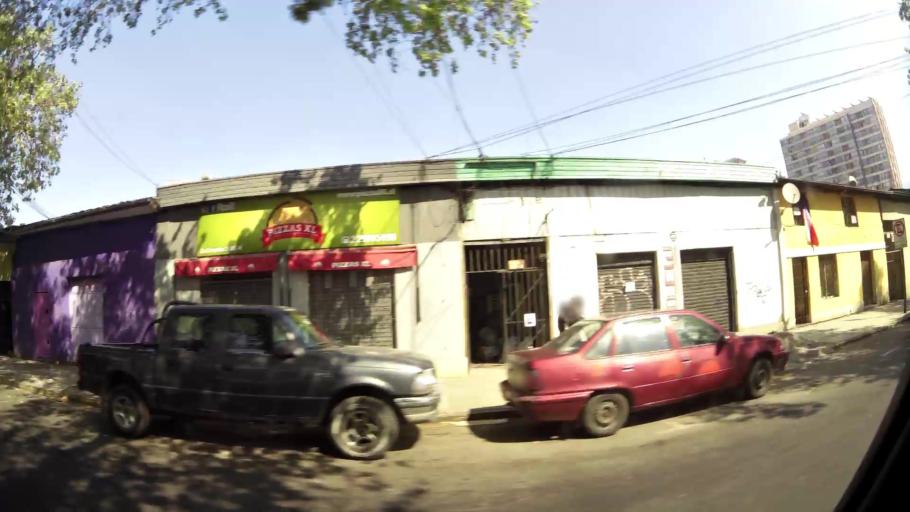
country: CL
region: Santiago Metropolitan
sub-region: Provincia de Santiago
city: Santiago
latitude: -33.4510
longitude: -70.6835
